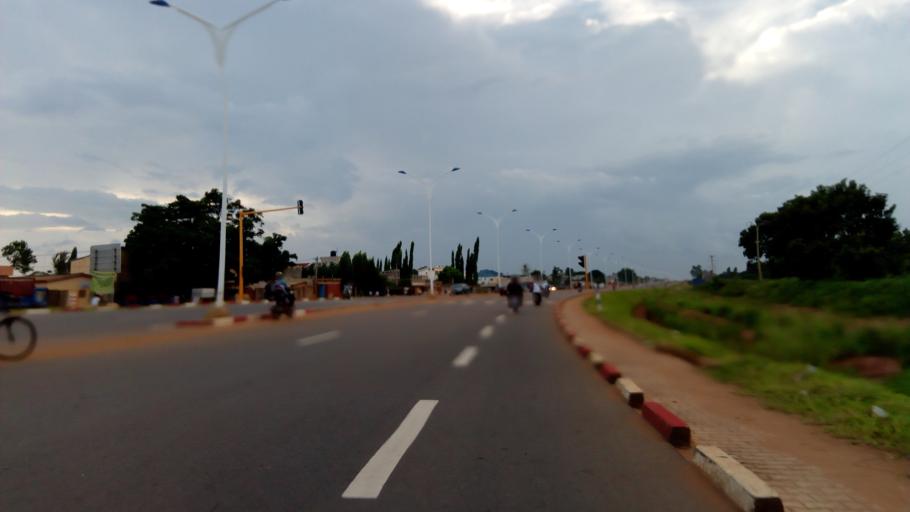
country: TG
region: Maritime
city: Lome
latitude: 6.2450
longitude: 1.1846
